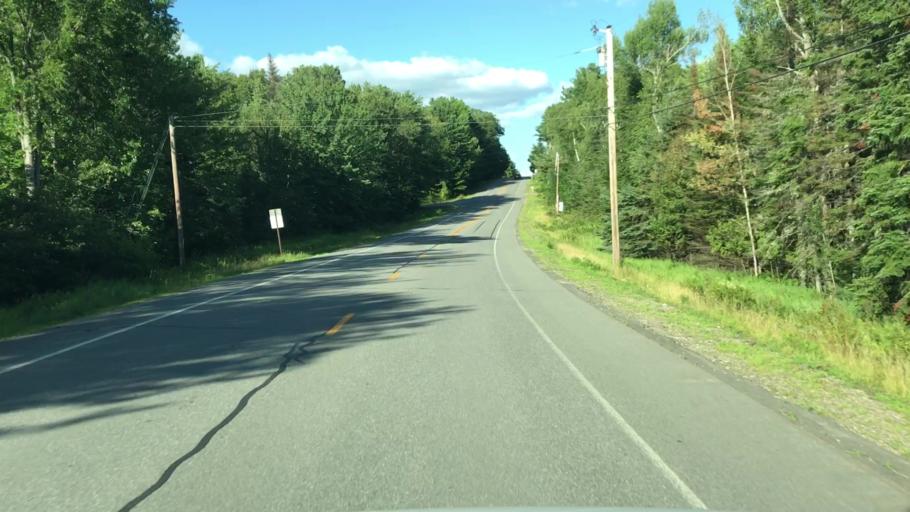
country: US
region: Maine
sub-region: Penobscot County
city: Lincoln
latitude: 45.3763
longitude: -68.4637
